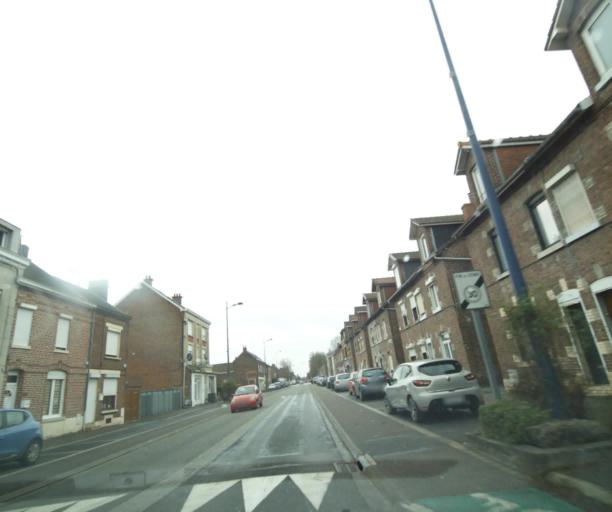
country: FR
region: Nord-Pas-de-Calais
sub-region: Departement du Nord
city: Crespin
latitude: 50.4109
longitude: 3.6632
